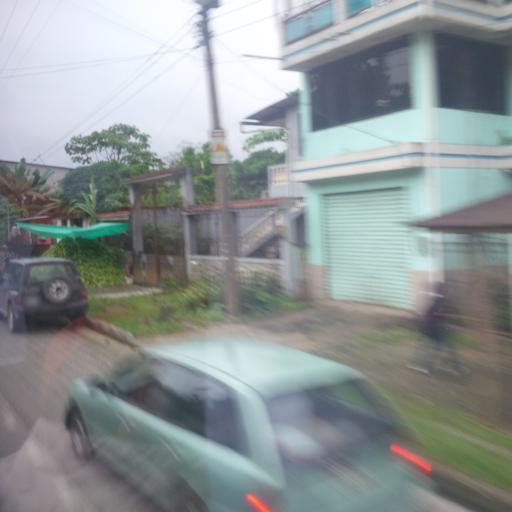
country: EC
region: Chimborazo
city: Alausi
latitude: -2.2010
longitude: -79.1230
